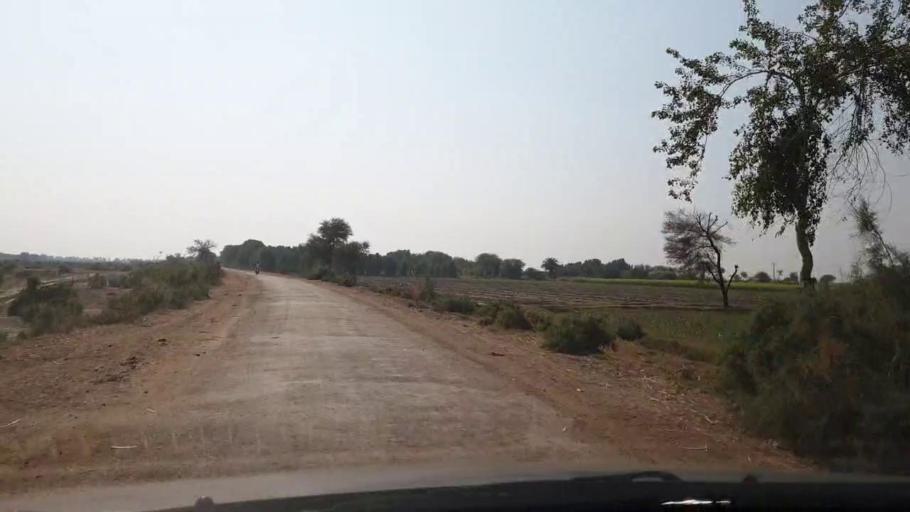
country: PK
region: Sindh
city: Jhol
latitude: 25.8418
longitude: 68.9877
